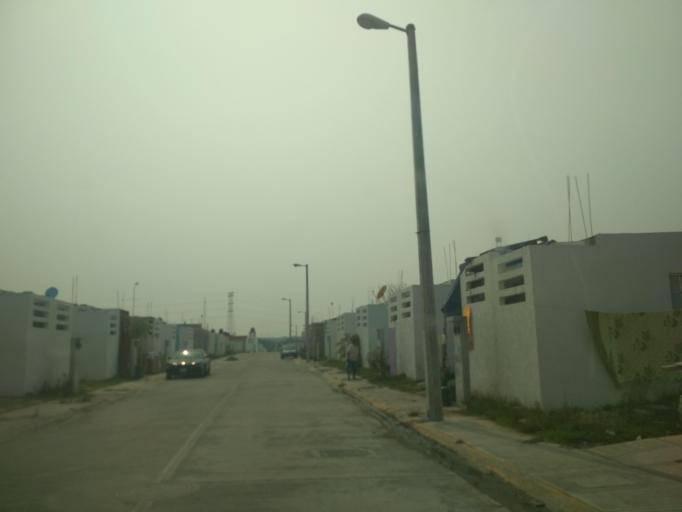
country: MX
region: Veracruz
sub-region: Veracruz
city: Las Amapolas
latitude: 19.1389
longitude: -96.2237
